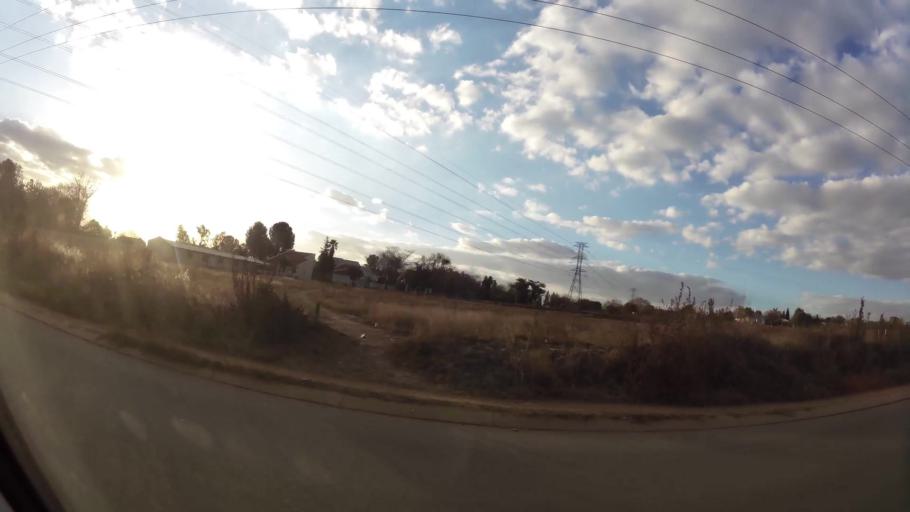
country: ZA
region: Gauteng
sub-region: City of Johannesburg Metropolitan Municipality
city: Diepsloot
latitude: -26.0043
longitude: 27.9770
